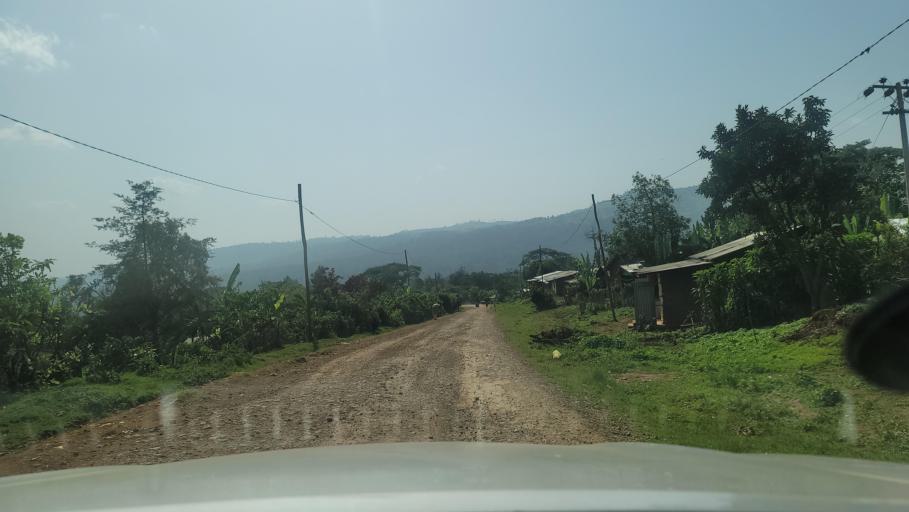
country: ET
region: Oromiya
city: Agaro
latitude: 7.7930
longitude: 36.4518
